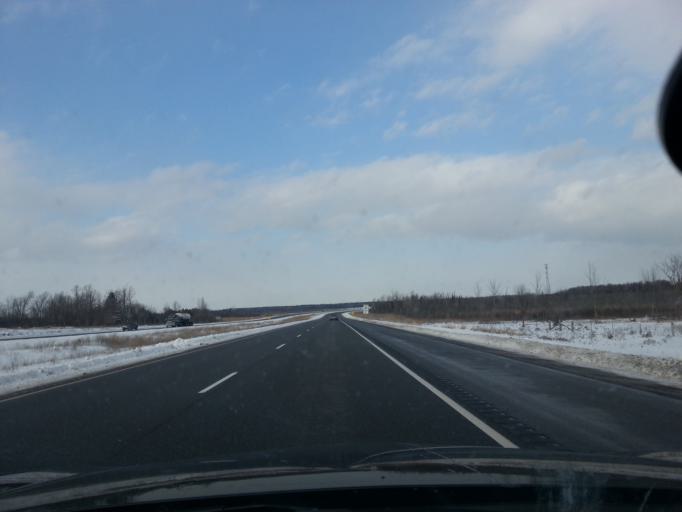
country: CA
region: Ontario
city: Carleton Place
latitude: 45.1906
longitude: -76.0450
